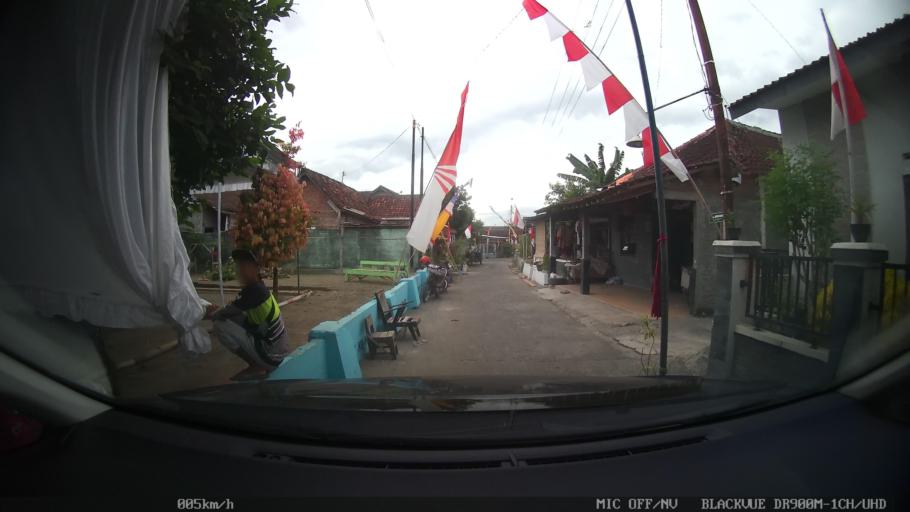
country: ID
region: Daerah Istimewa Yogyakarta
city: Depok
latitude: -7.8152
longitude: 110.4191
